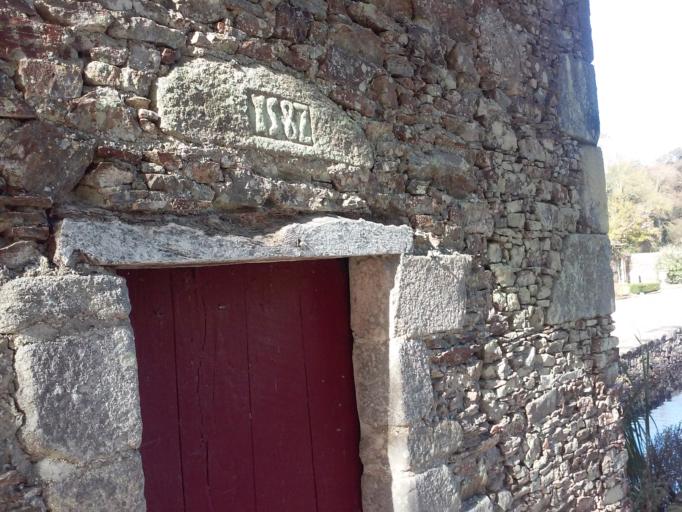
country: FR
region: Pays de la Loire
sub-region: Departement de la Vendee
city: Saint-Andre-Treize-Voies
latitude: 46.8792
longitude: -1.4040
